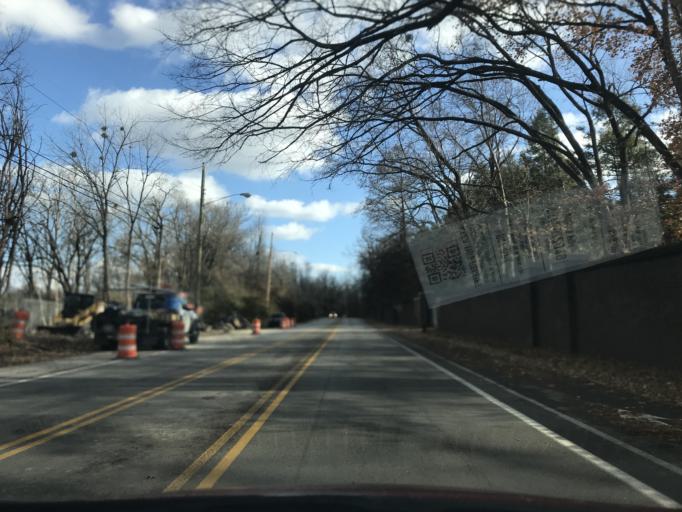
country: US
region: Indiana
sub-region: Clark County
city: Jeffersonville
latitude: 38.2499
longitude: -85.7149
